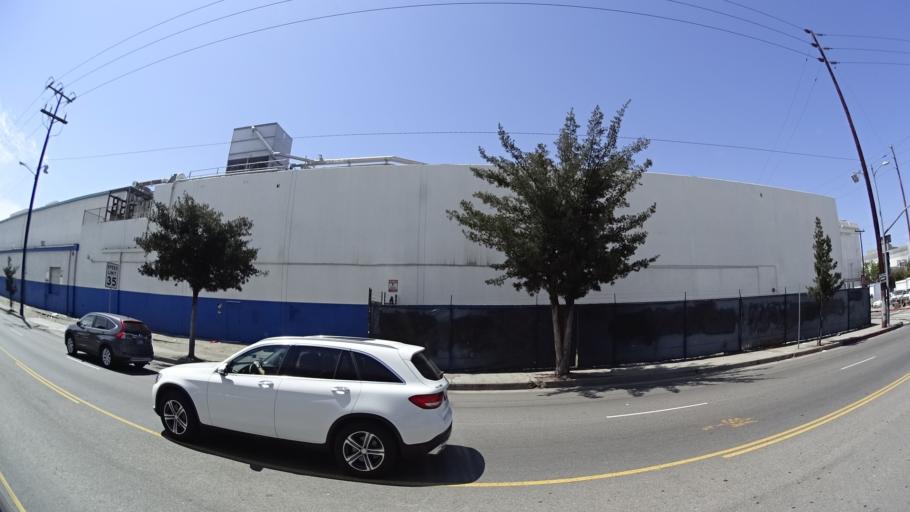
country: US
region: California
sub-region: Los Angeles County
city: Los Angeles
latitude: 34.0429
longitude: -118.2383
